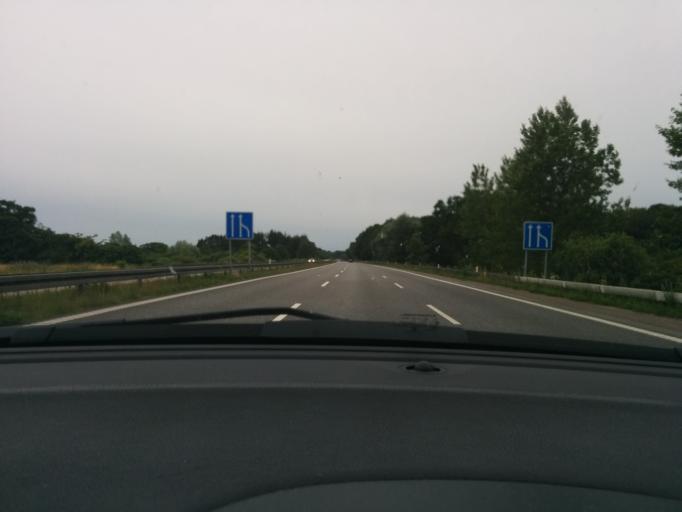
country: DK
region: Zealand
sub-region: Faxe Kommune
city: Ronnede
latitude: 55.2435
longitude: 11.9857
